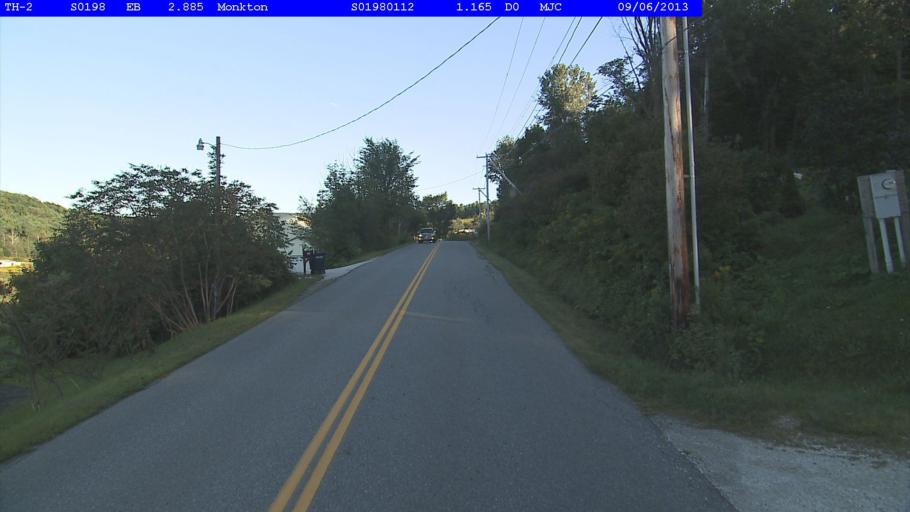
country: US
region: Vermont
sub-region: Chittenden County
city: Hinesburg
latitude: 44.2494
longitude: -73.1752
